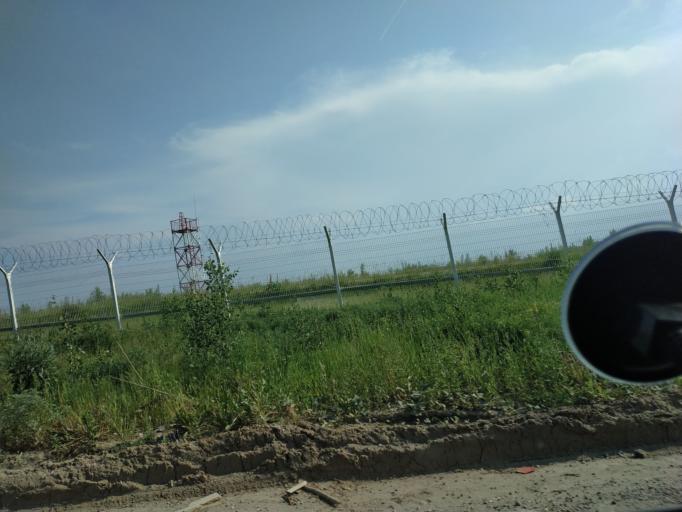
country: RU
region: Moskovskaya
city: Yakovlevskoye
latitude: 55.4309
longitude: 37.9095
